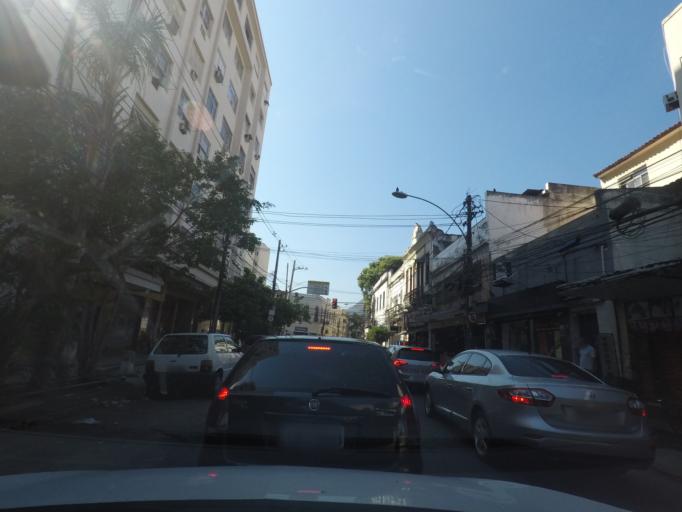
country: BR
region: Rio de Janeiro
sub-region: Rio De Janeiro
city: Rio de Janeiro
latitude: -22.9173
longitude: -43.2120
